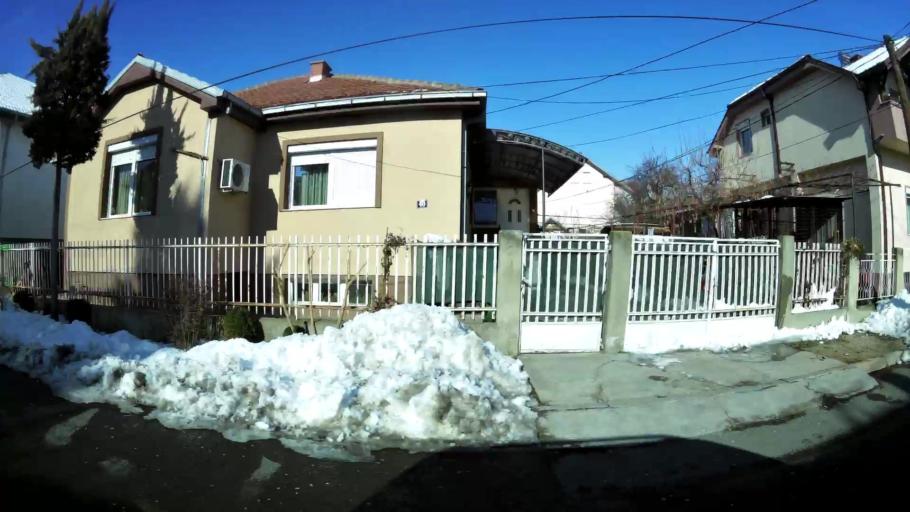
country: MK
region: Saraj
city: Saraj
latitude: 42.0073
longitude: 21.3482
